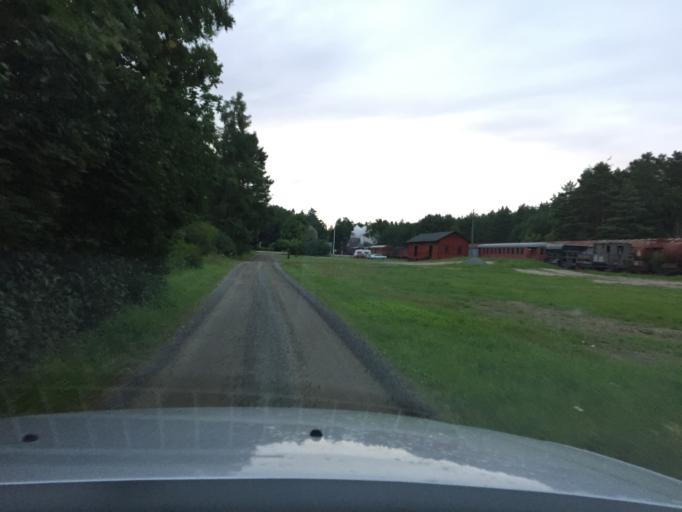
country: SE
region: Skane
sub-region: Kristianstads Kommun
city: Degeberga
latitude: 55.7330
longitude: 14.1246
